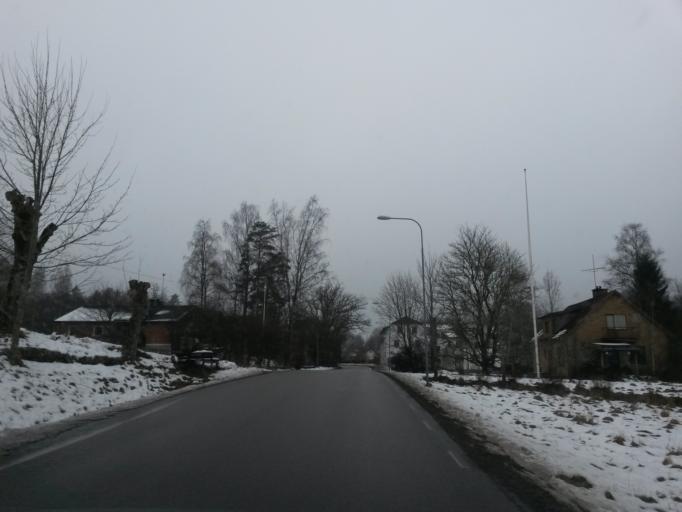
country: SE
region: Vaestra Goetaland
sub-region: Tranemo Kommun
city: Langhem
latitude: 57.6971
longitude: 13.3021
